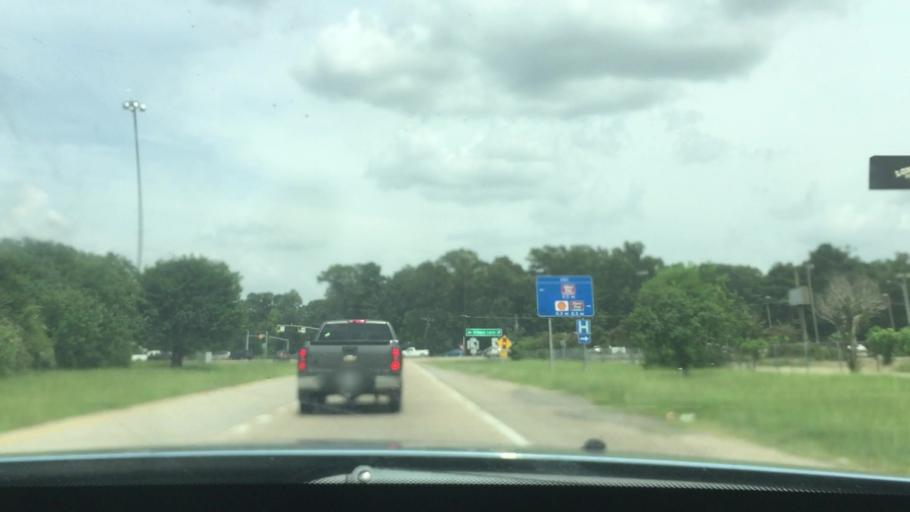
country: US
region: Louisiana
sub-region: East Baton Rouge Parish
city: Shenandoah
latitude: 30.4414
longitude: -91.0093
